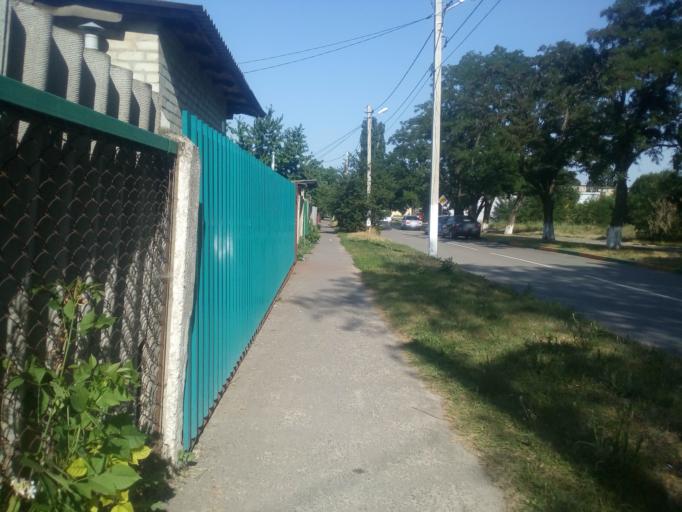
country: RU
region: Rostov
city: Sholokhovskiy
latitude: 48.2804
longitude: 41.0512
